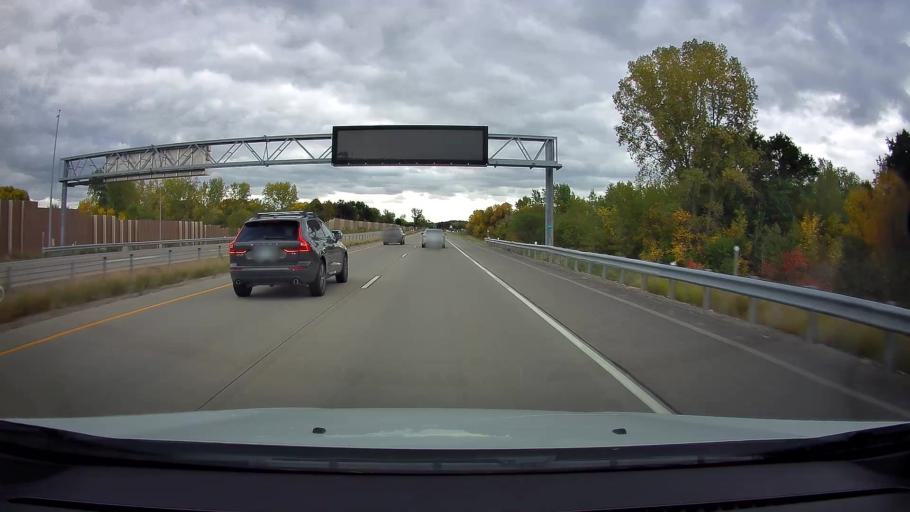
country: US
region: Minnesota
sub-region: Ramsey County
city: North Oaks
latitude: 45.1112
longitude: -93.0495
